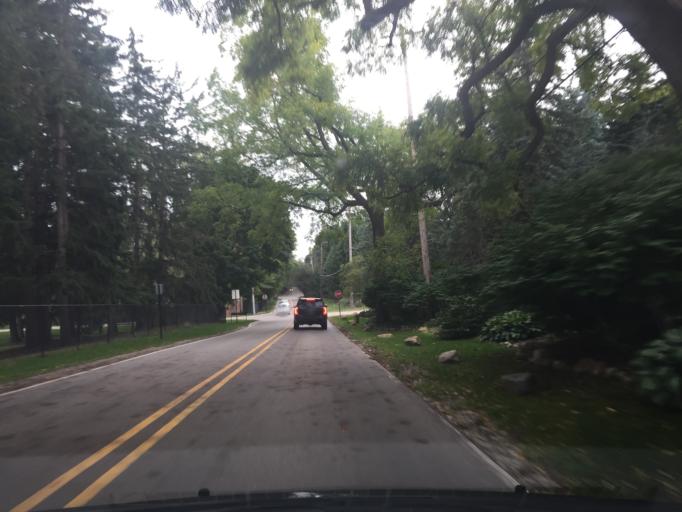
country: US
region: Michigan
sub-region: Oakland County
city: Bloomfield Hills
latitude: 42.5756
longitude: -83.2567
